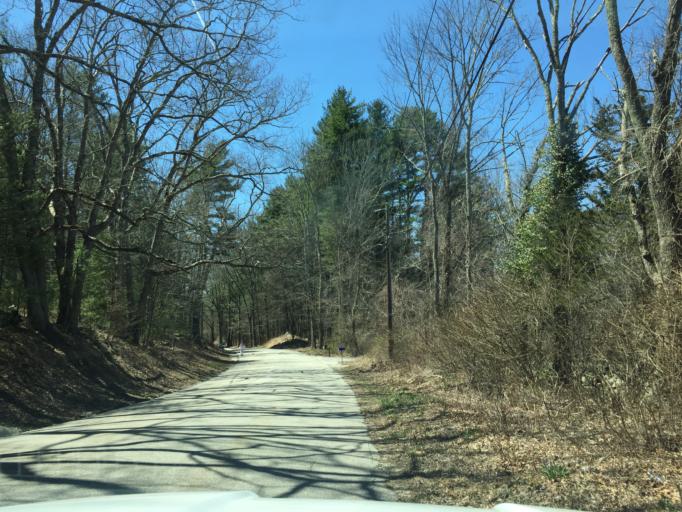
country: US
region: Connecticut
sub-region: Windham County
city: Quinebaug
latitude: 41.9825
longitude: -71.9545
